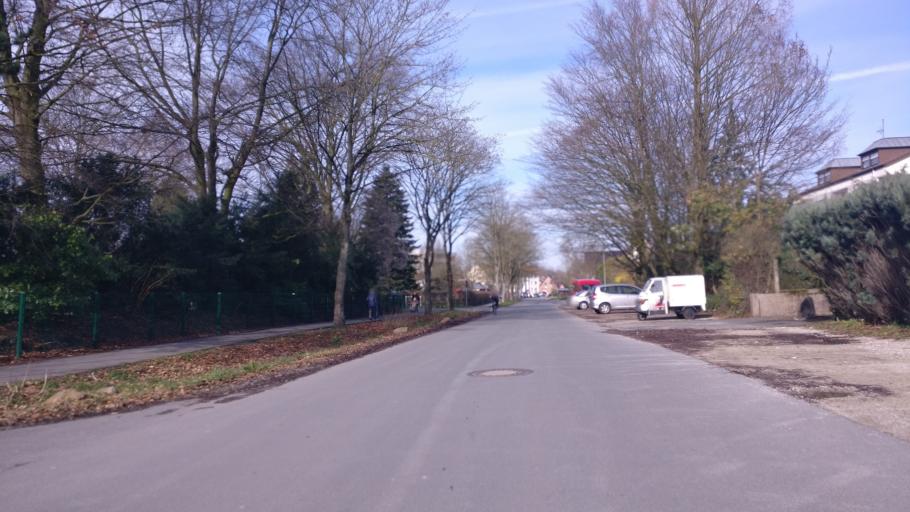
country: DE
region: North Rhine-Westphalia
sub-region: Regierungsbezirk Detmold
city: Lage
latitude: 51.9944
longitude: 8.7877
